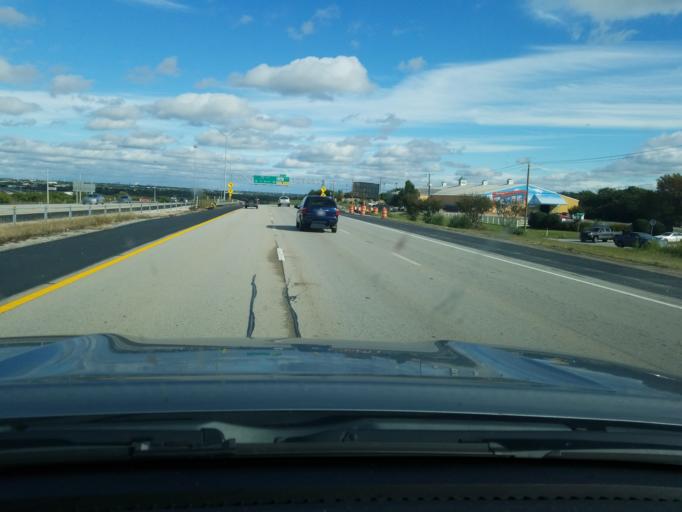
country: US
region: Texas
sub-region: Tarrant County
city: White Settlement
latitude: 32.7205
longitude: -97.5270
